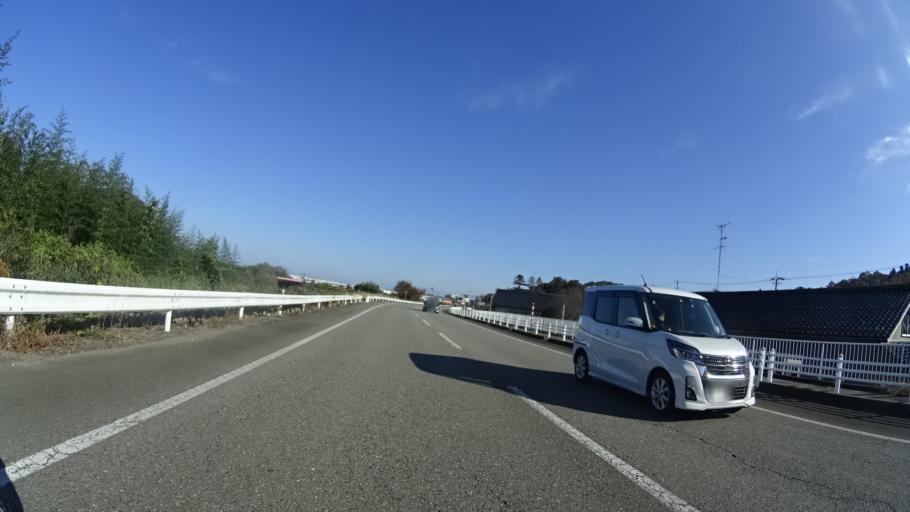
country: JP
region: Ishikawa
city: Komatsu
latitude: 36.3128
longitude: 136.3886
